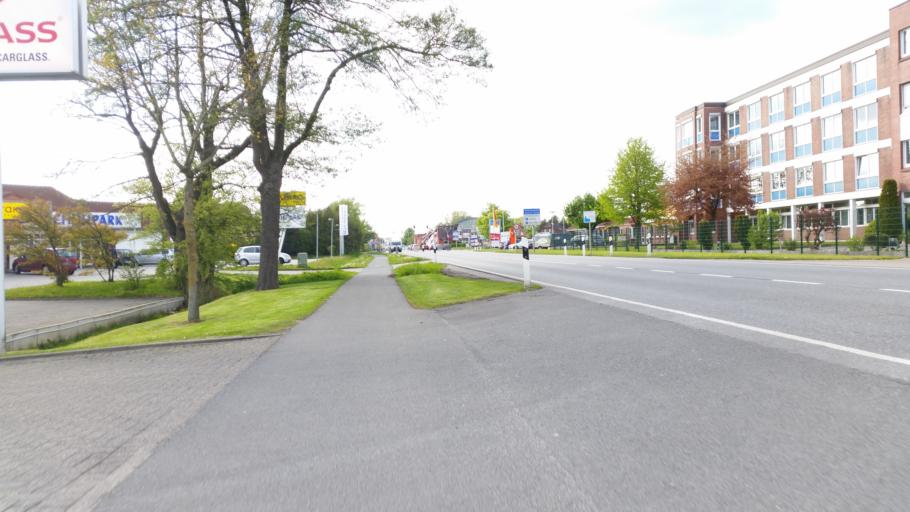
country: DE
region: Lower Saxony
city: Aurich
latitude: 53.4602
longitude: 7.4930
